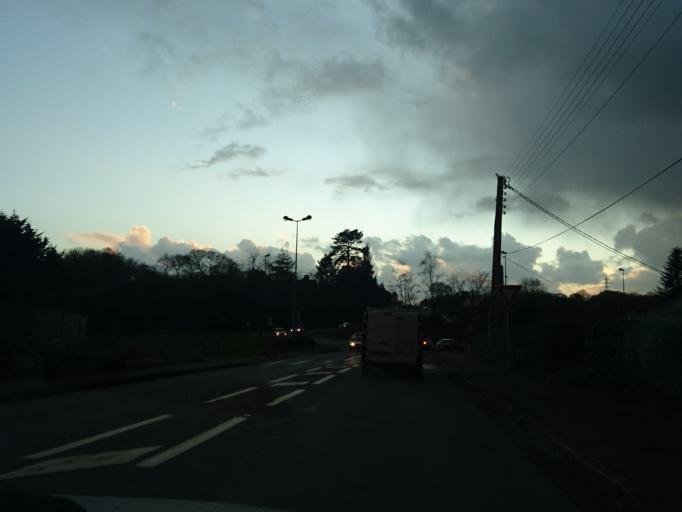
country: FR
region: Brittany
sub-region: Departement du Finistere
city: Guipavas
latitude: 48.4287
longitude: -4.4112
